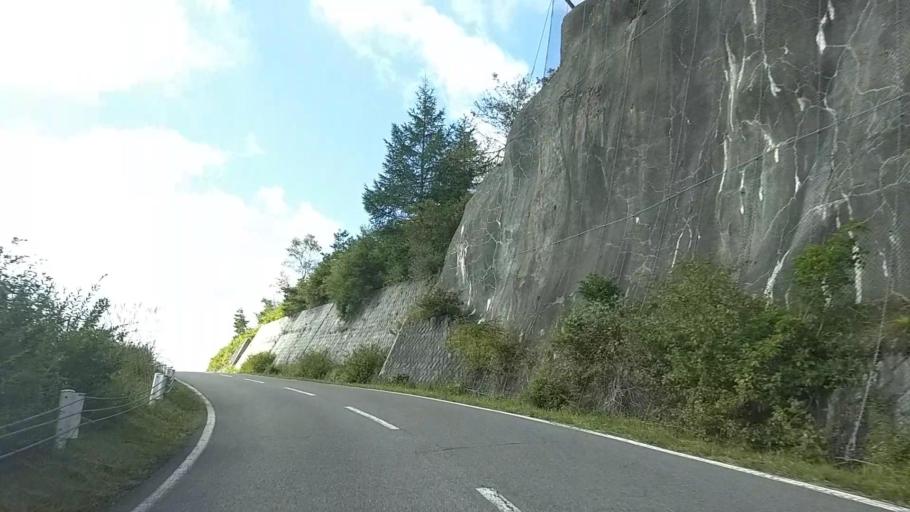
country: JP
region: Nagano
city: Suwa
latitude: 36.0941
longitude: 138.1929
